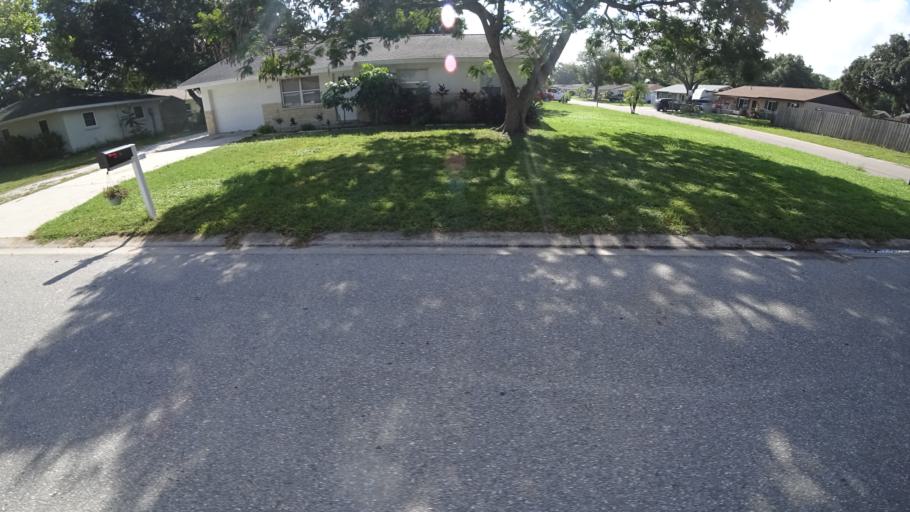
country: US
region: Florida
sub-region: Manatee County
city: Ellenton
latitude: 27.4982
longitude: -82.4794
